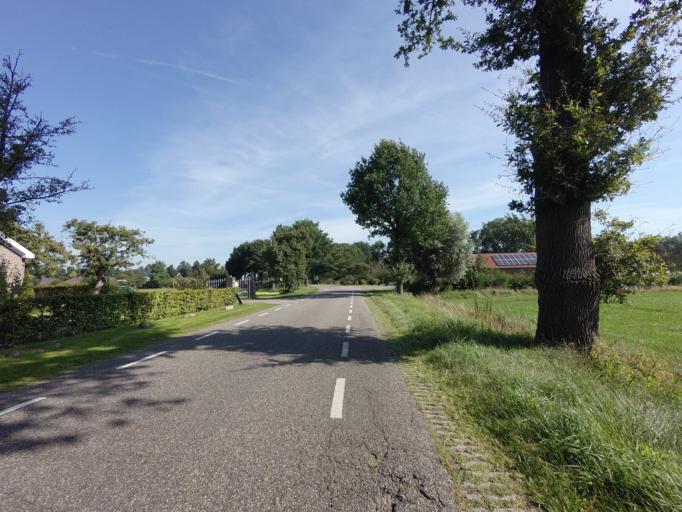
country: NL
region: Gelderland
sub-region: Oost Gelre
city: Lichtenvoorde
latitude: 52.0438
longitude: 6.5459
